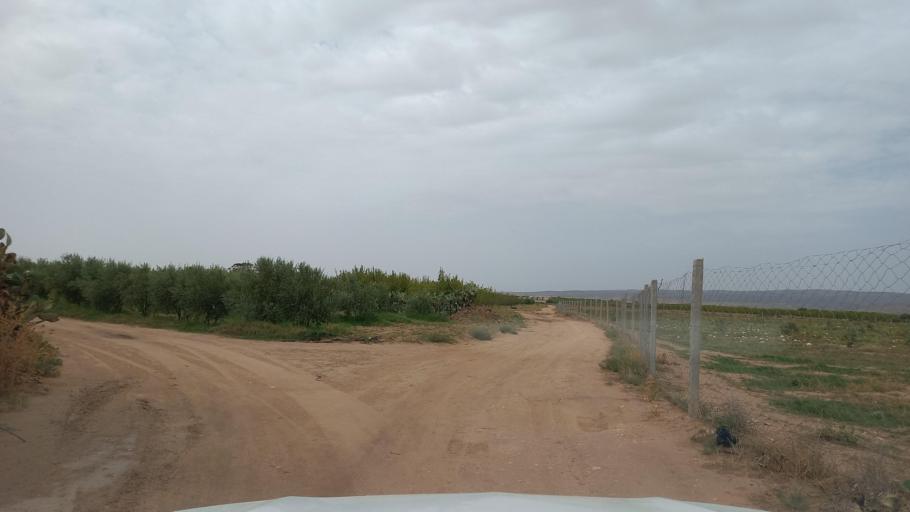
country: TN
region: Al Qasrayn
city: Kasserine
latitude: 35.2867
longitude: 9.0250
